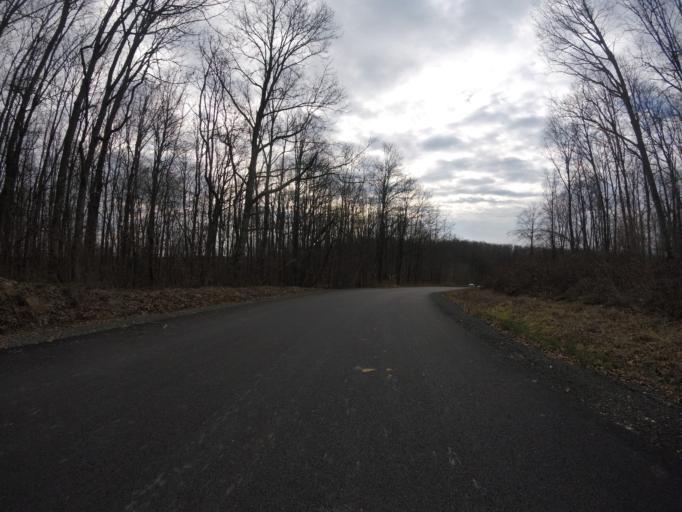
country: HR
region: Sisacko-Moslavacka
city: Glina
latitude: 45.4887
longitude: 16.0457
